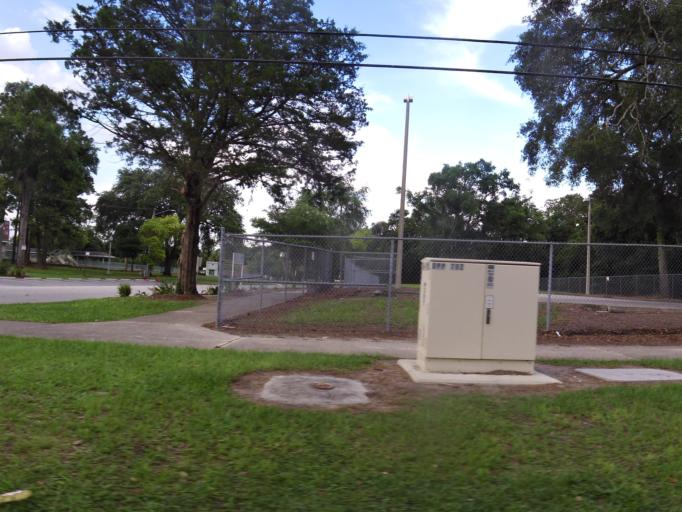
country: US
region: Florida
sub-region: Duval County
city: Jacksonville
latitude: 30.3182
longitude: -81.6925
